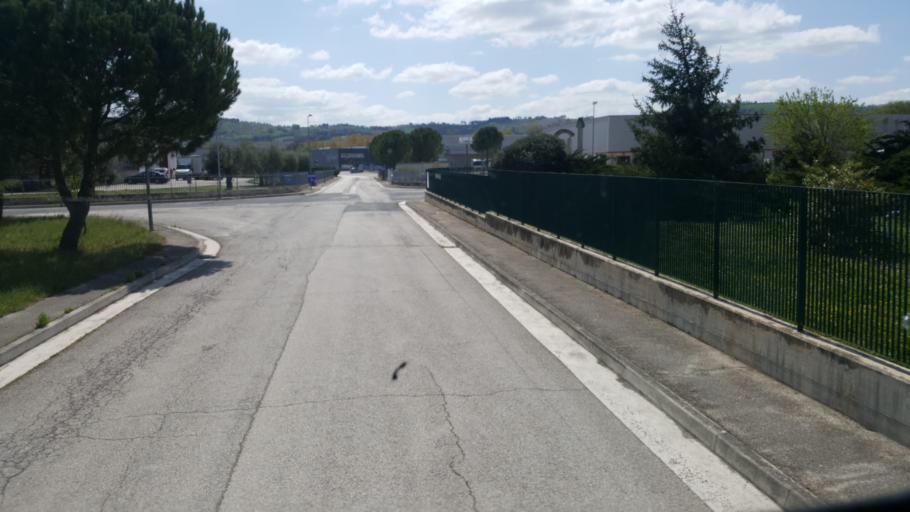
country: IT
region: The Marches
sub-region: Provincia di Macerata
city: Montecassiano
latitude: 43.3547
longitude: 13.4577
